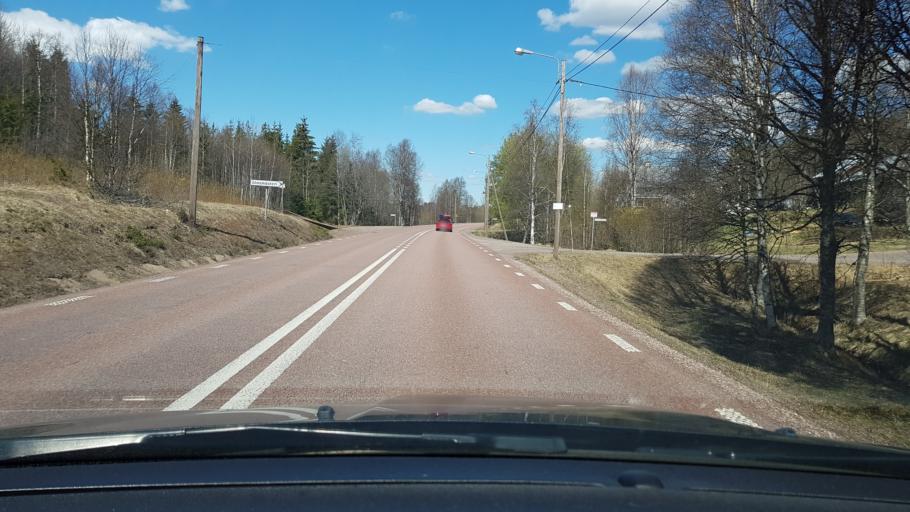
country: SE
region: Dalarna
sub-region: Malung-Saelens kommun
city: Malung
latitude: 61.0759
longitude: 13.3275
